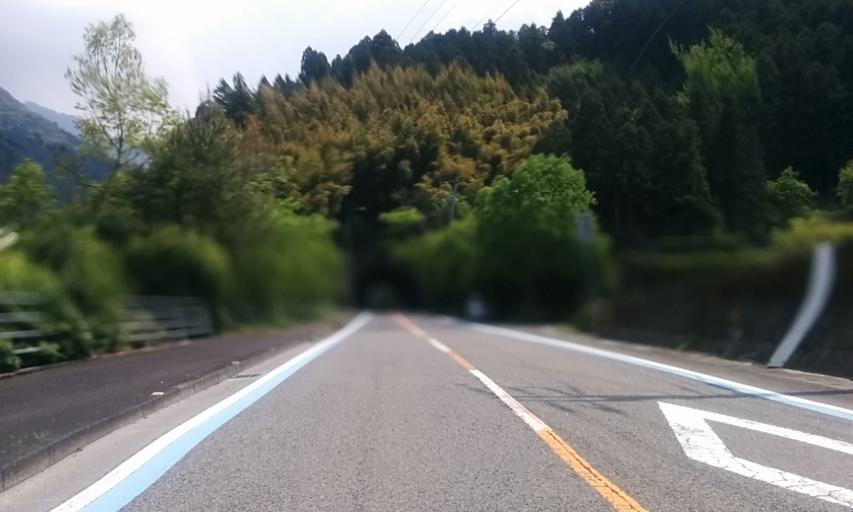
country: JP
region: Ehime
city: Saijo
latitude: 33.8465
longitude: 133.2162
